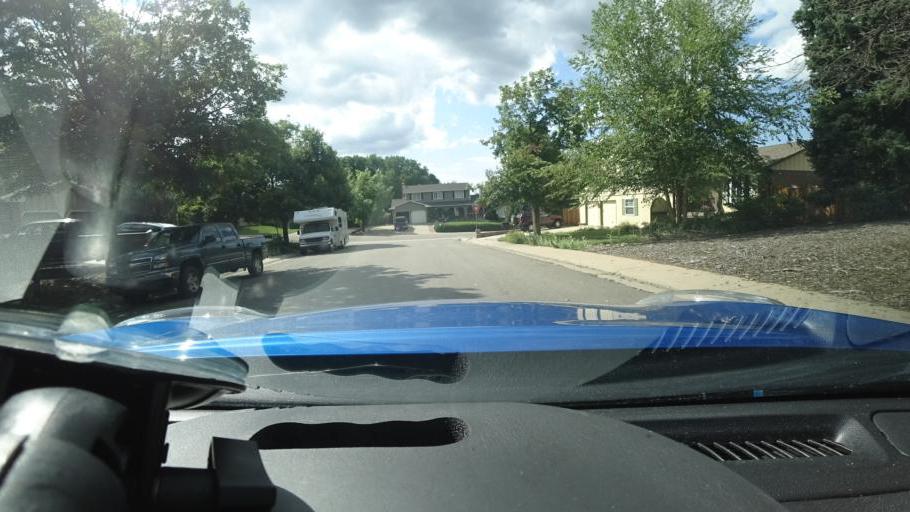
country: US
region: Colorado
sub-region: Adams County
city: Aurora
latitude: 39.6839
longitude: -104.8529
